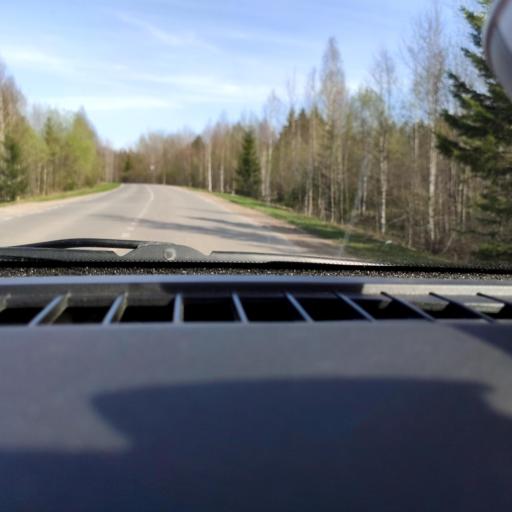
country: RU
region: Perm
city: Kondratovo
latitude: 58.2501
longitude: 56.1171
